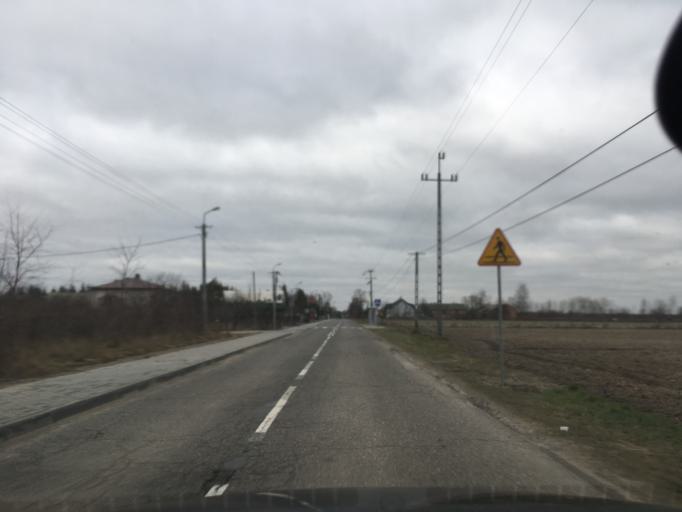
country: PL
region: Masovian Voivodeship
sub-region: Powiat piaseczynski
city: Lesznowola
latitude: 52.0444
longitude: 20.9520
